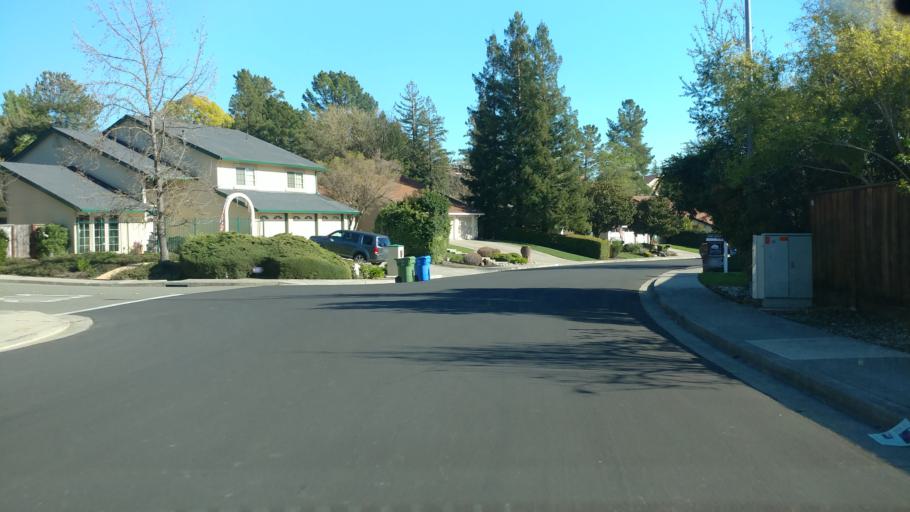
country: US
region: California
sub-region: Contra Costa County
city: San Ramon
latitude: 37.8035
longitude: -121.9728
